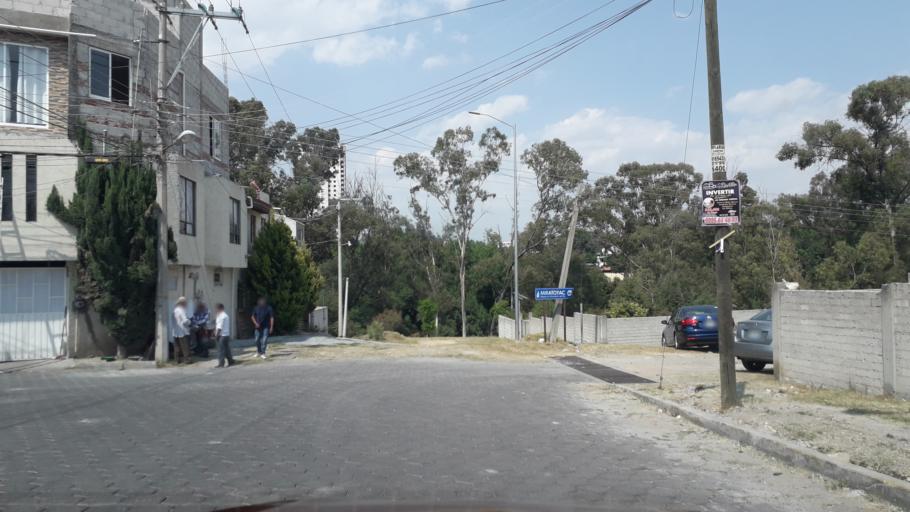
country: MX
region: Puebla
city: Puebla
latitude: 19.0296
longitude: -98.2254
